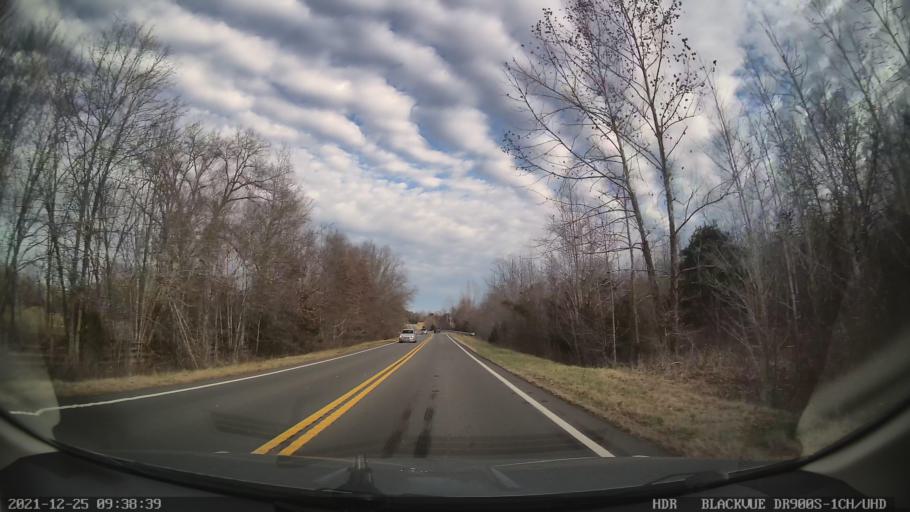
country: US
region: Virginia
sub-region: Goochland County
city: Goochland
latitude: 37.7920
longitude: -77.8730
